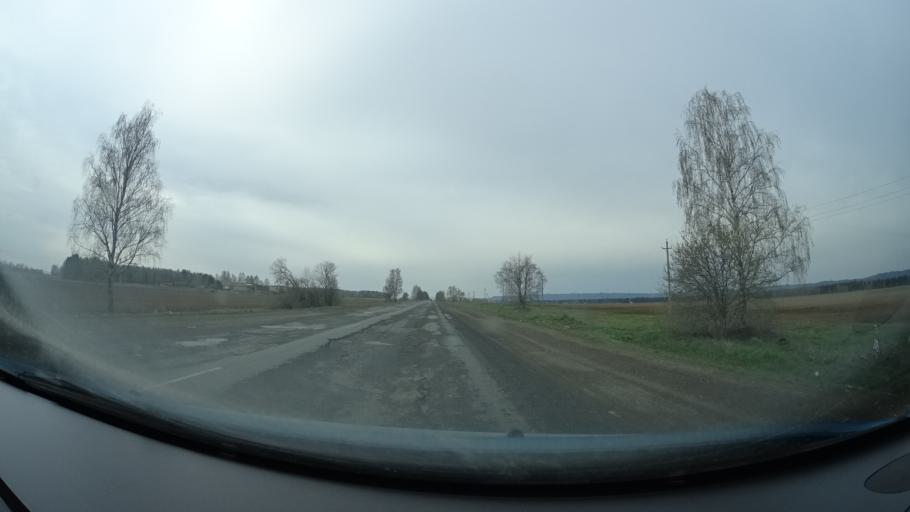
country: RU
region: Perm
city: Ust'-Kachka
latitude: 58.0600
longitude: 55.6114
